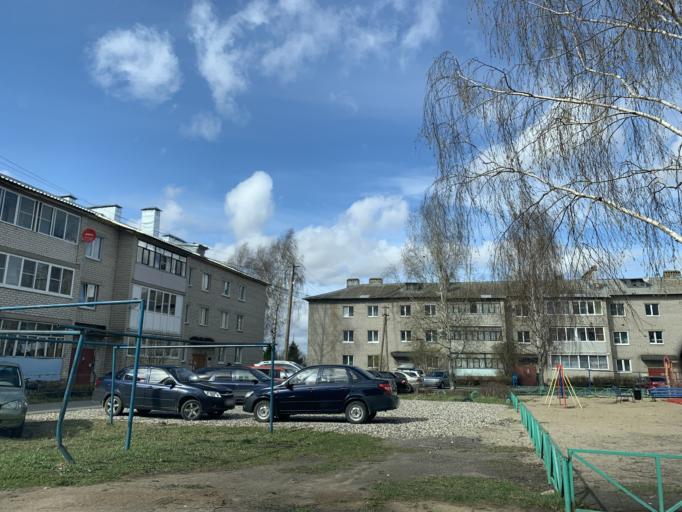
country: RU
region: Jaroslavl
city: Tunoshna
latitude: 57.6593
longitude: 40.0650
